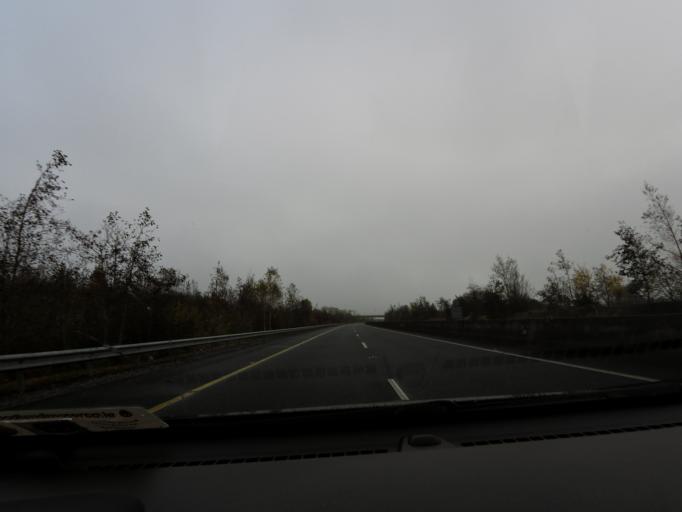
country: IE
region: Connaught
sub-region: County Galway
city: Ballinasloe
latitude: 53.3062
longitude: -8.3277
